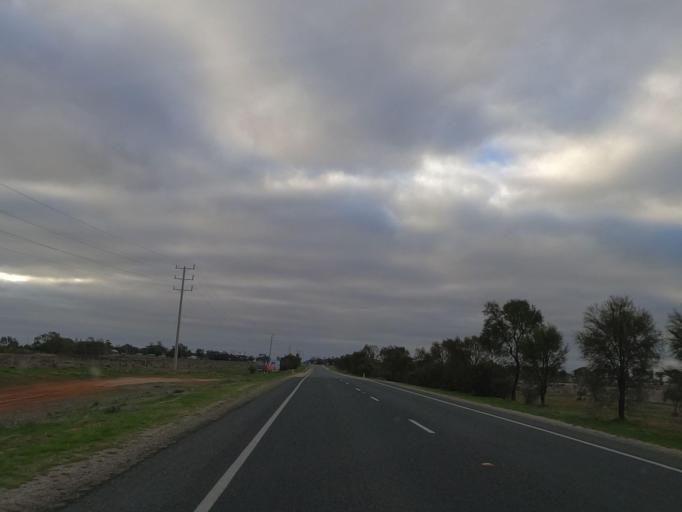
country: AU
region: Victoria
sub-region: Swan Hill
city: Swan Hill
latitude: -35.6171
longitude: 143.8034
